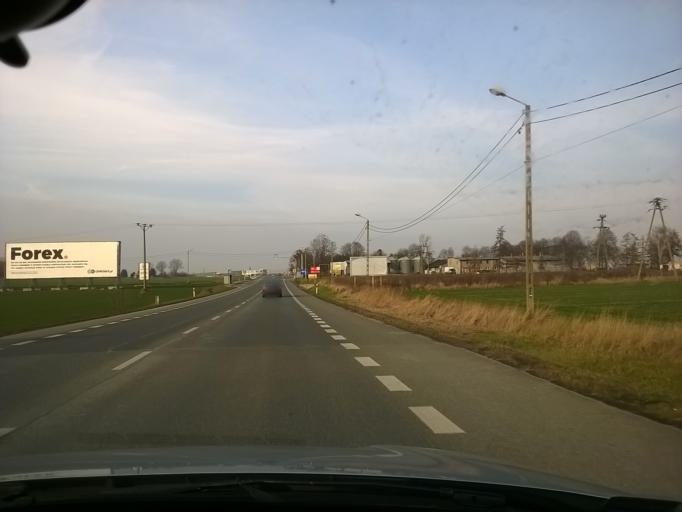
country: PL
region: Silesian Voivodeship
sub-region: Powiat gliwicki
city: Przyszowice
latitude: 50.2551
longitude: 18.7337
